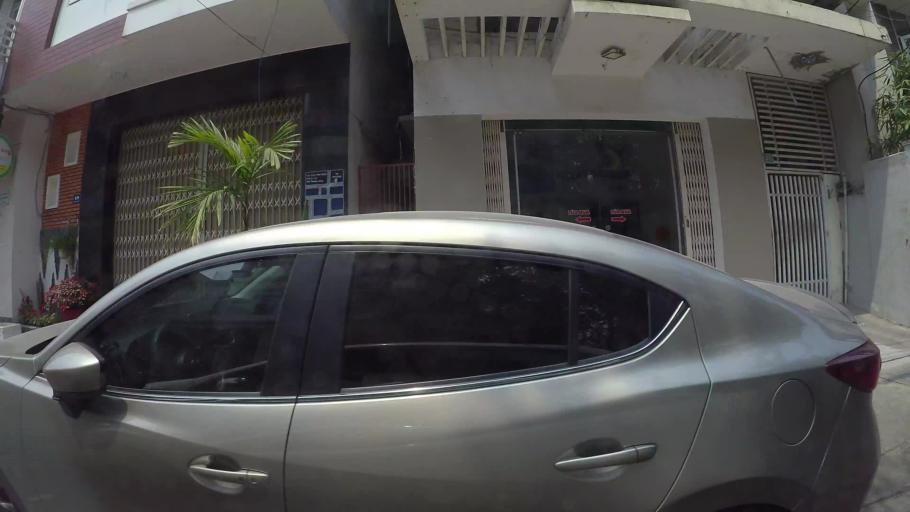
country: VN
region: Da Nang
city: Da Nang
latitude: 16.0801
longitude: 108.2155
